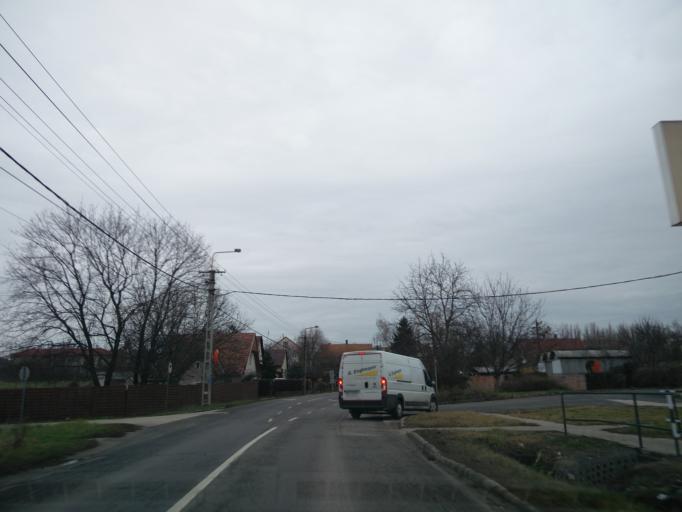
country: HU
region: Pest
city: Gyomro
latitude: 47.4154
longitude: 19.4037
